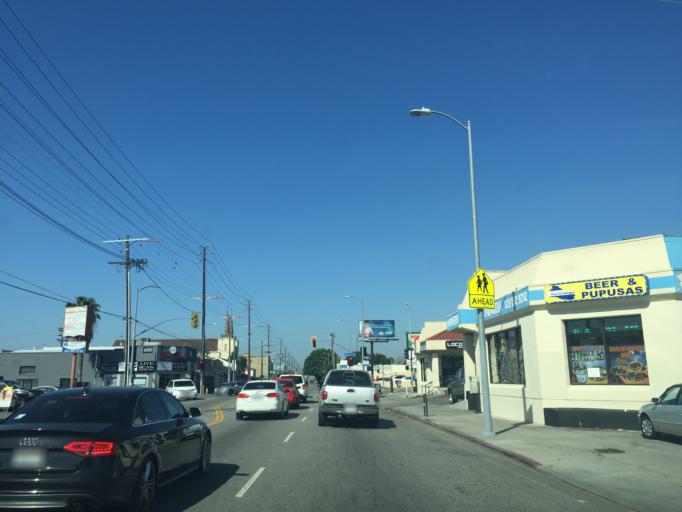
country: US
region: California
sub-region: Los Angeles County
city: Silver Lake
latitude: 34.0909
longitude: -118.2954
